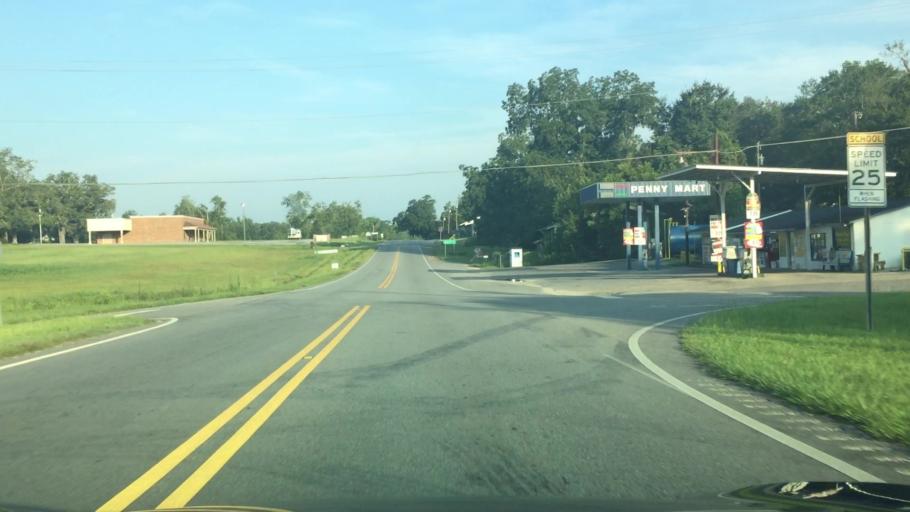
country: US
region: Alabama
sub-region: Covington County
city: Florala
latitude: 31.0107
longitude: -86.3499
